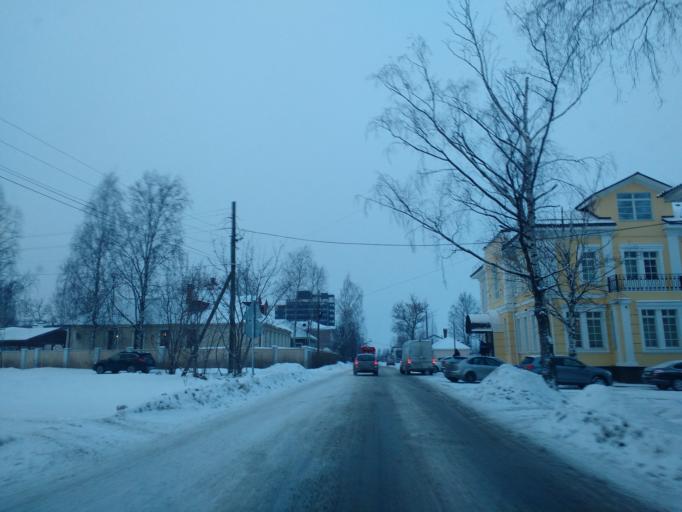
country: RU
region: Republic of Karelia
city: Petrozavodsk
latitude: 61.7966
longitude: 34.3719
